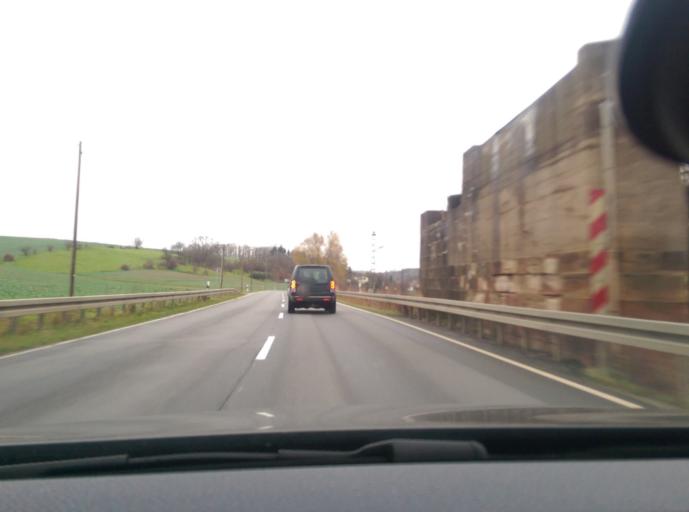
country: DE
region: Hesse
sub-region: Regierungsbezirk Kassel
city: Eschwege
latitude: 51.1711
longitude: 9.9896
